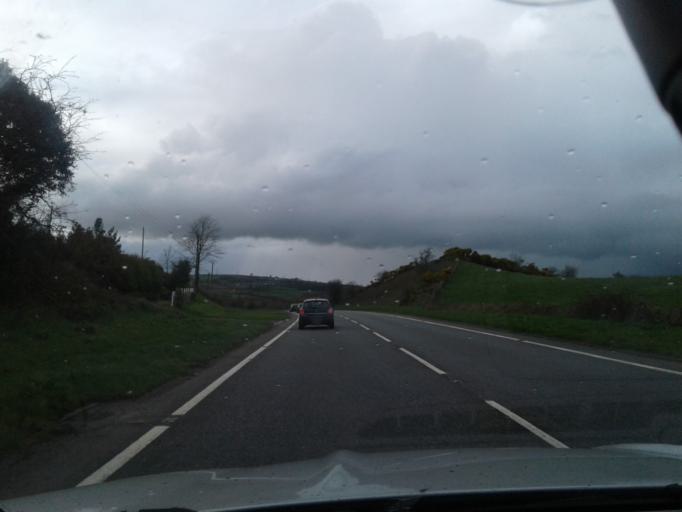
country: GB
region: Northern Ireland
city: Newtownstewart
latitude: 54.7339
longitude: -7.4242
